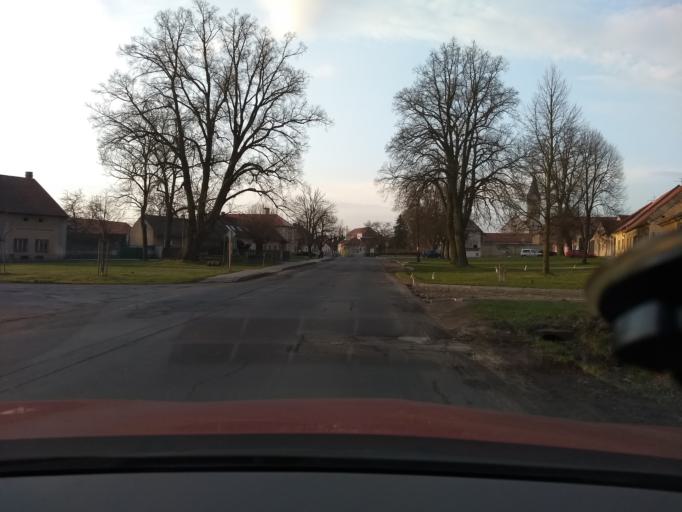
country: CZ
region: Central Bohemia
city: Rudna
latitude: 50.0439
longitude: 14.1856
